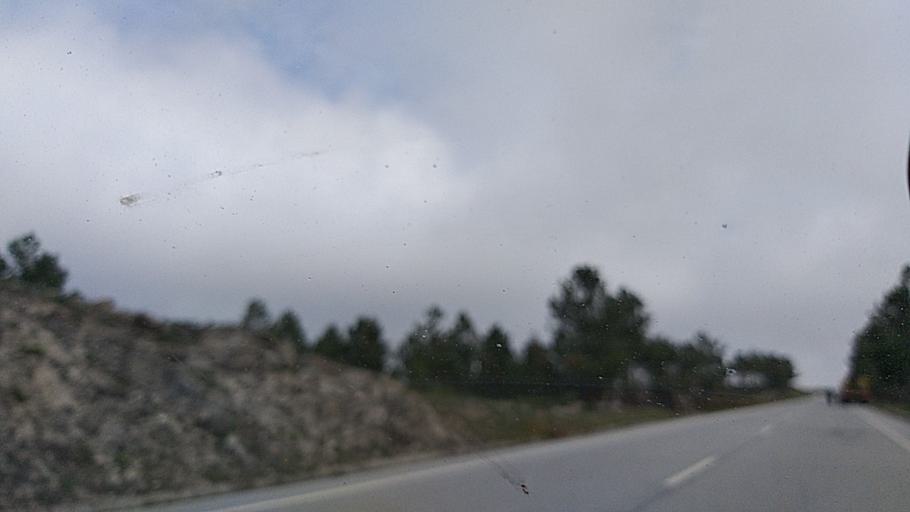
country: PT
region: Guarda
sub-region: Aguiar da Beira
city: Aguiar da Beira
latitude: 40.7580
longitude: -7.5026
